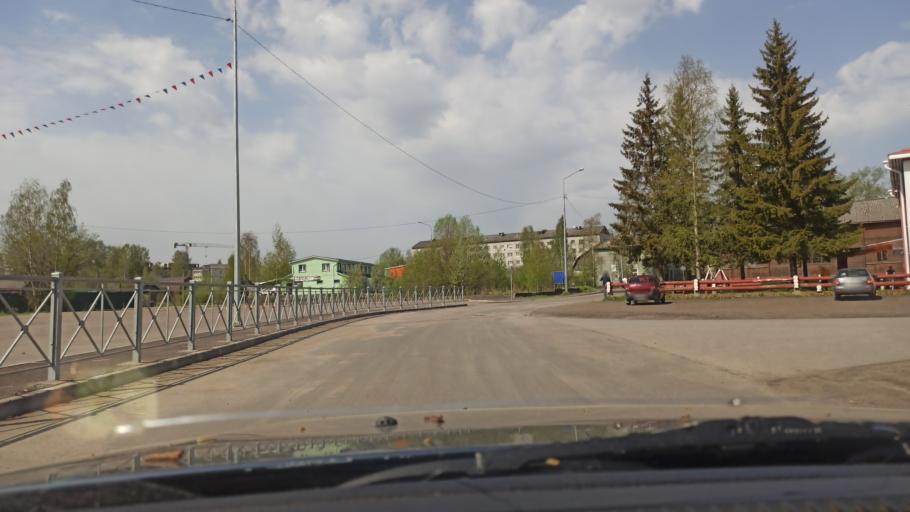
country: RU
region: Republic of Karelia
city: Lakhdenpokh'ya
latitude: 61.5174
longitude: 30.2037
